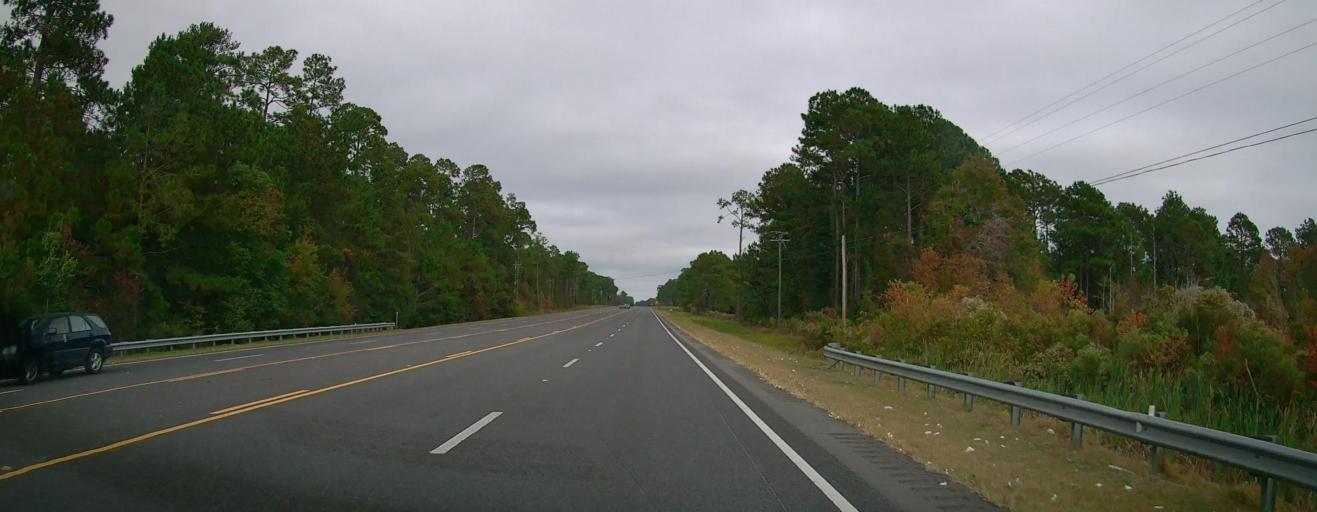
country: US
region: Georgia
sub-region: Colquitt County
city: Moultrie
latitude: 31.0832
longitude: -83.8155
